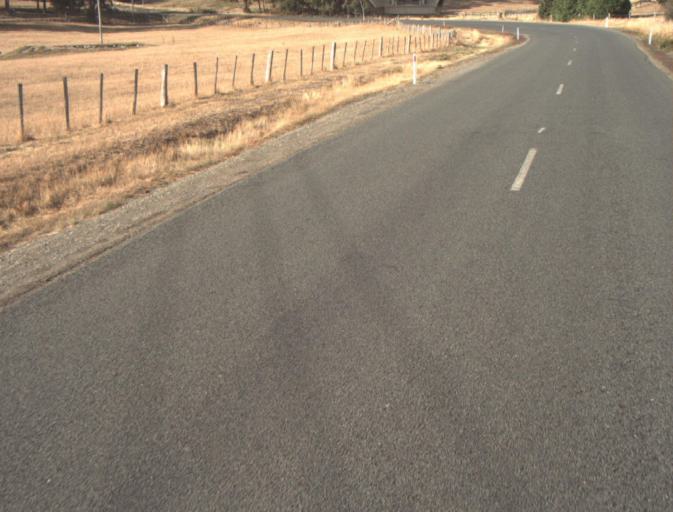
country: AU
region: Tasmania
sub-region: Launceston
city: Mayfield
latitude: -41.1987
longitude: 147.2180
